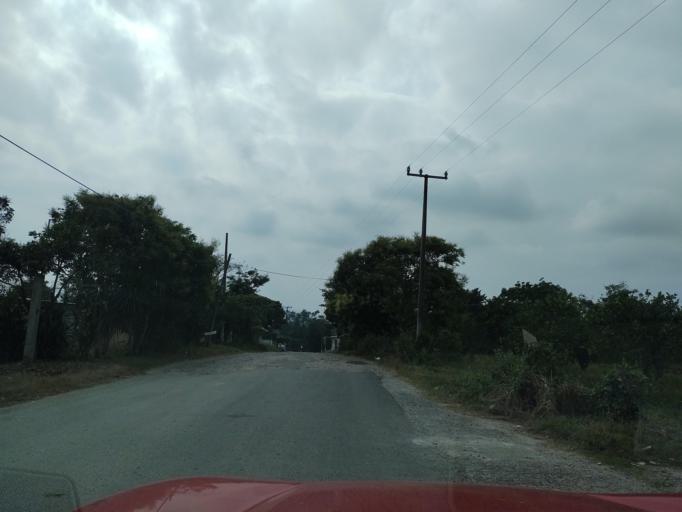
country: MX
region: Veracruz
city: Agua Dulce
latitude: 20.3430
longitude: -97.2924
